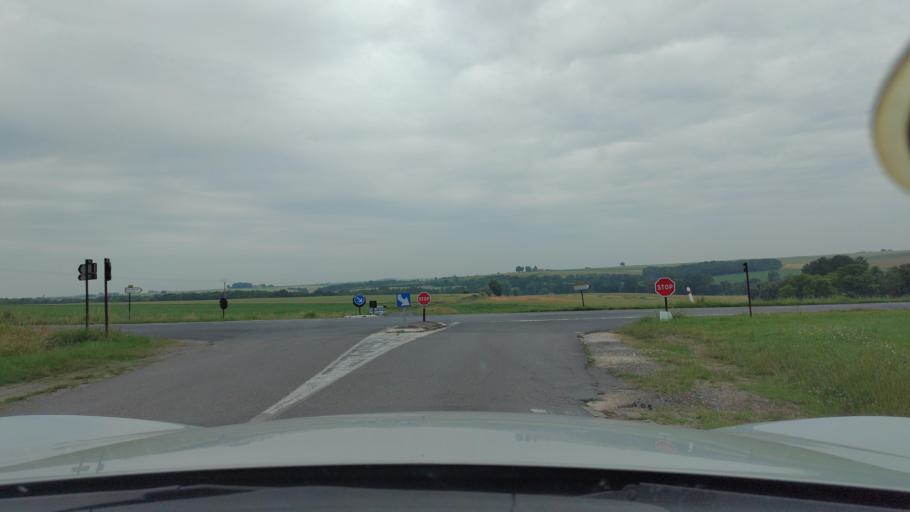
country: FR
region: Ile-de-France
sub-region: Departement de Seine-et-Marne
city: Varreddes
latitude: 49.0328
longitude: 2.8966
